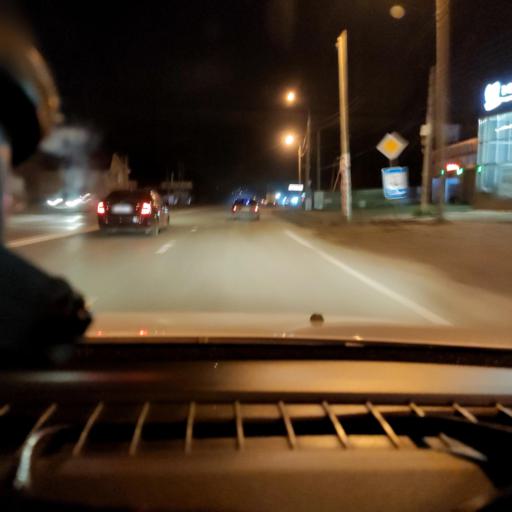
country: RU
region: Samara
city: Volzhskiy
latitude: 53.4241
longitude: 50.1246
